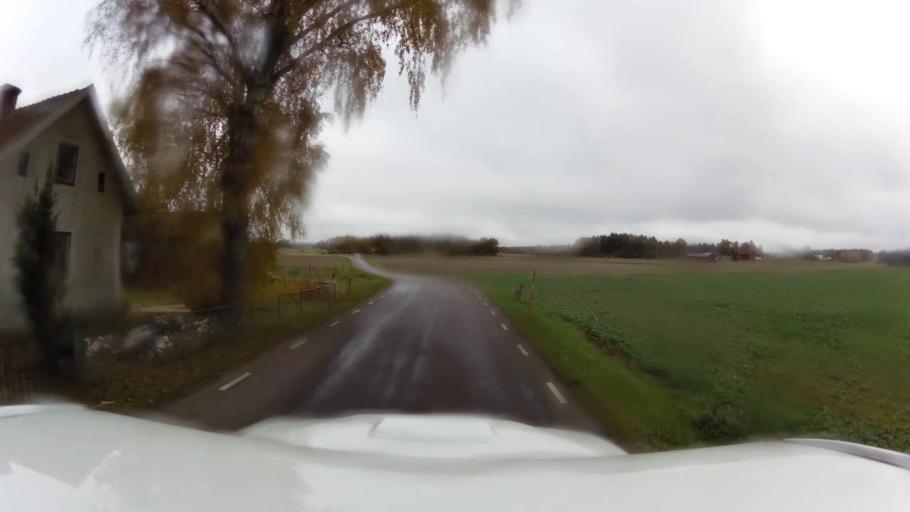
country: SE
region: OEstergoetland
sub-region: Linkopings Kommun
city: Linghem
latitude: 58.4569
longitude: 15.8305
